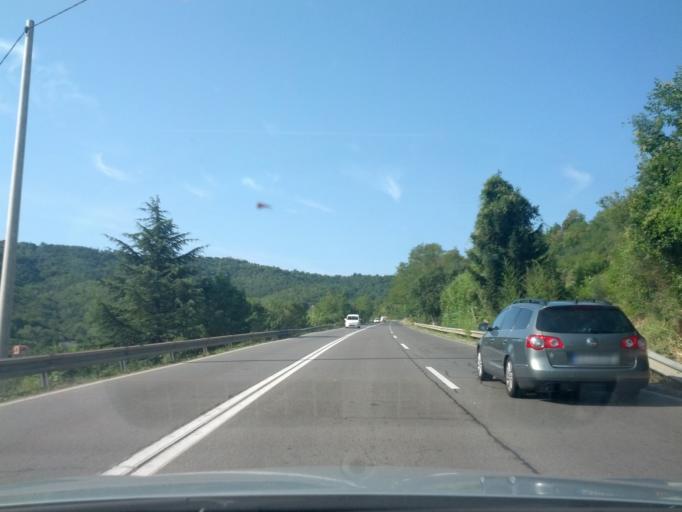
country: SI
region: Koper-Capodistria
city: Koper
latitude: 45.5152
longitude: 13.7231
